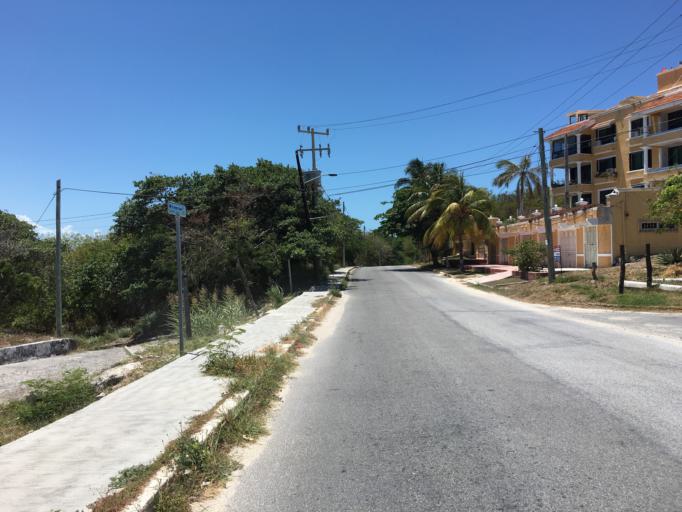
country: MX
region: Quintana Roo
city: Isla Mujeres
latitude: 21.2140
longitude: -86.7235
